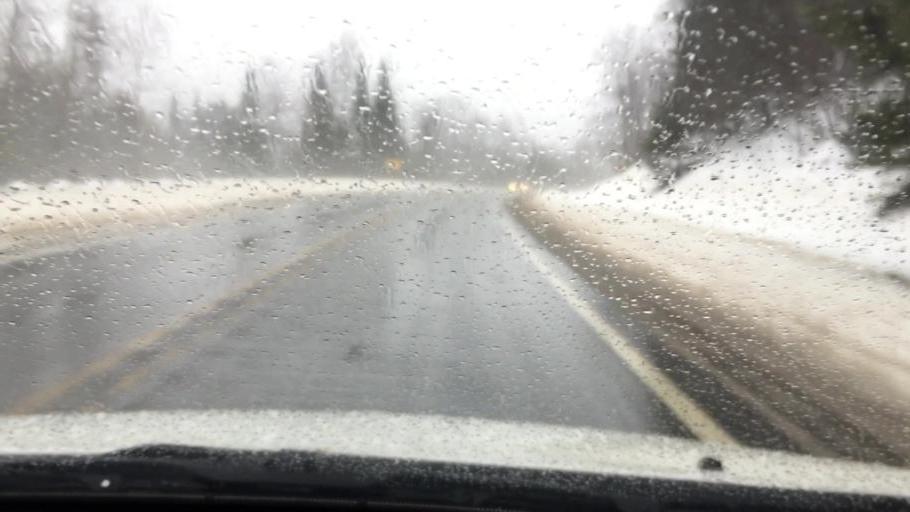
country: US
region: Michigan
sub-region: Antrim County
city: Mancelona
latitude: 44.9983
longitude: -85.0620
